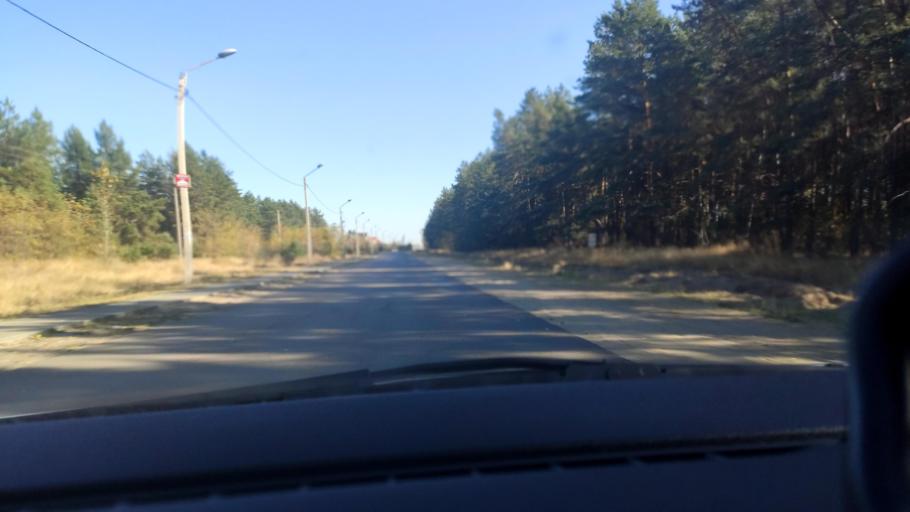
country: RU
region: Voronezj
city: Pridonskoy
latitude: 51.6252
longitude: 39.0840
